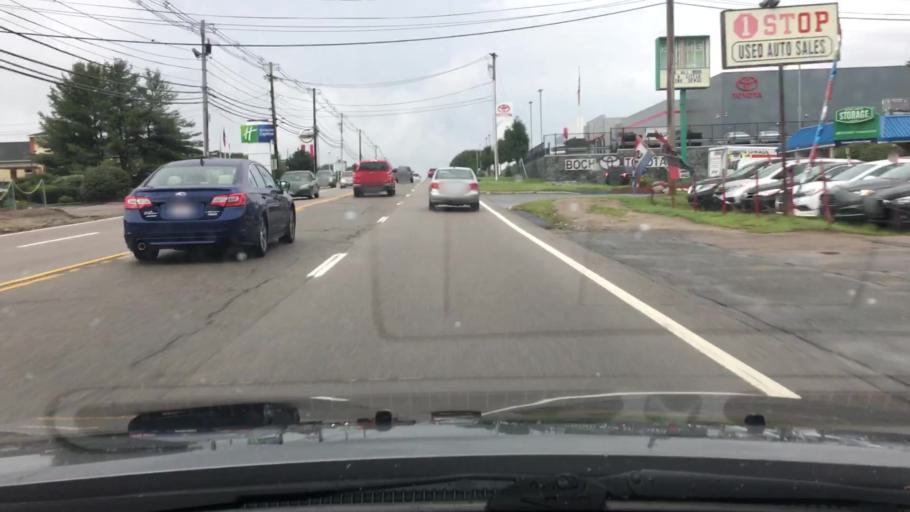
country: US
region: Massachusetts
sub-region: Norfolk County
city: Plainville
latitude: 41.9579
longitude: -71.3423
